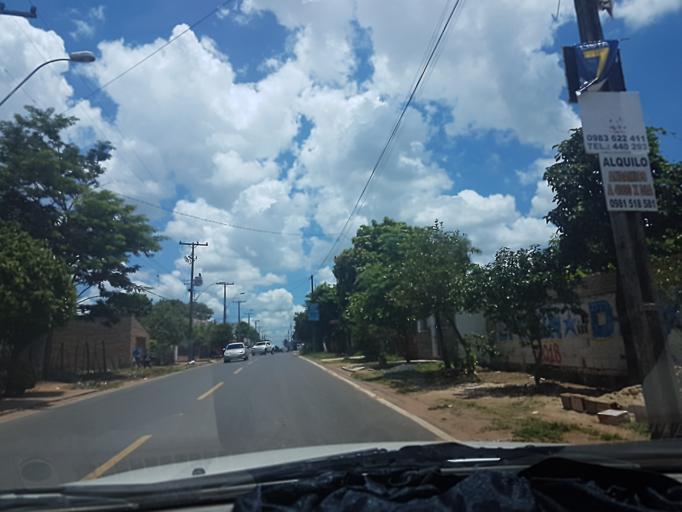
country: PY
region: Central
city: Limpio
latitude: -25.2072
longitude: -57.5174
